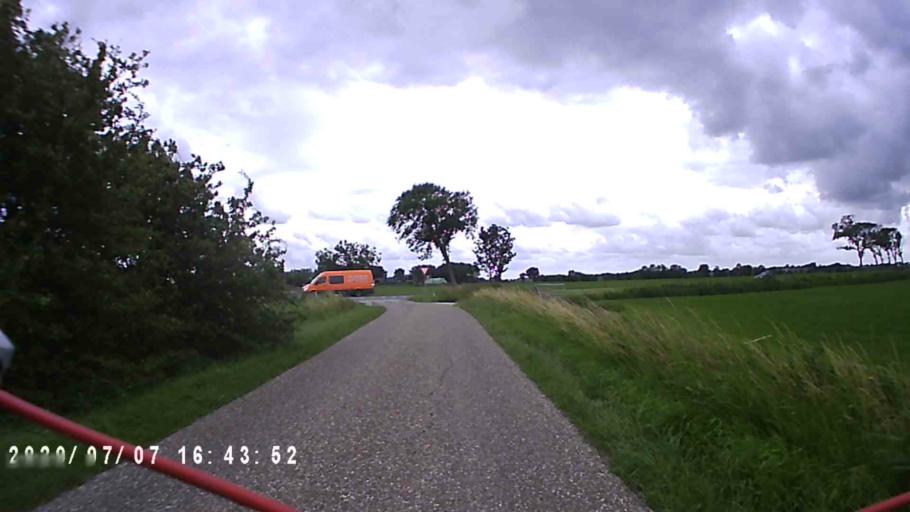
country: NL
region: Groningen
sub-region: Gemeente Winsum
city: Winsum
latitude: 53.3385
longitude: 6.5463
